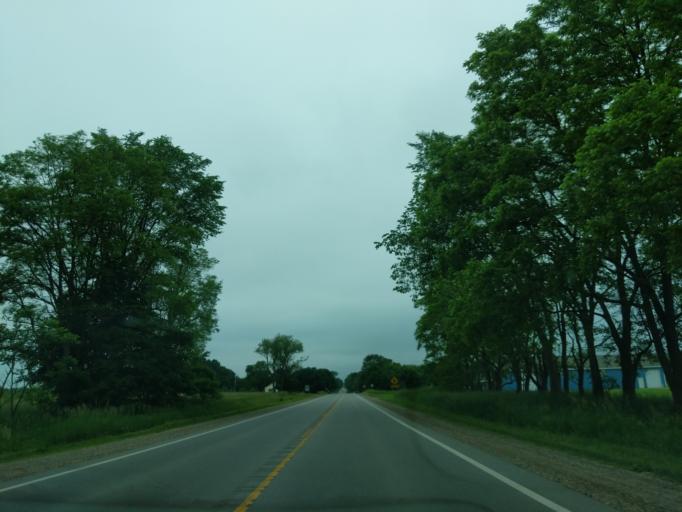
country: US
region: Michigan
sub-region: Branch County
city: Quincy
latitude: 41.9485
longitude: -84.8213
